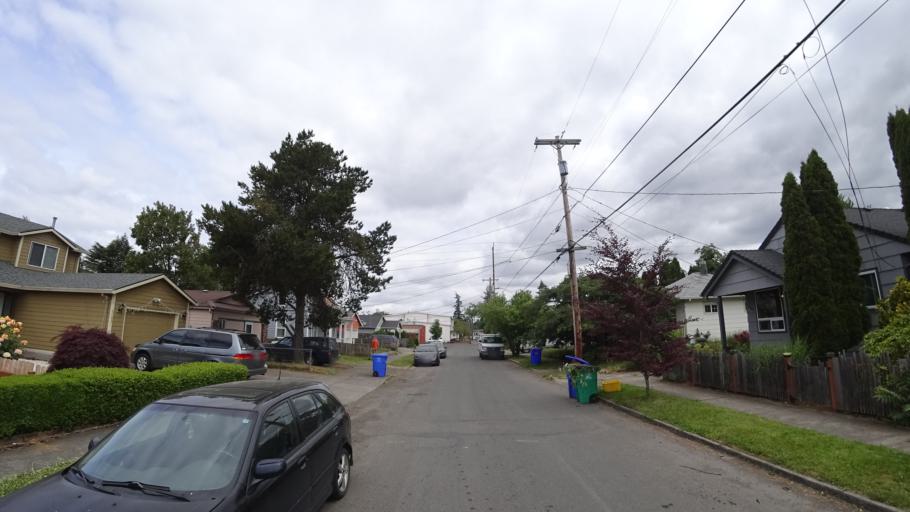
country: US
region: Oregon
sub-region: Multnomah County
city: Lents
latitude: 45.4785
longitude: -122.5726
